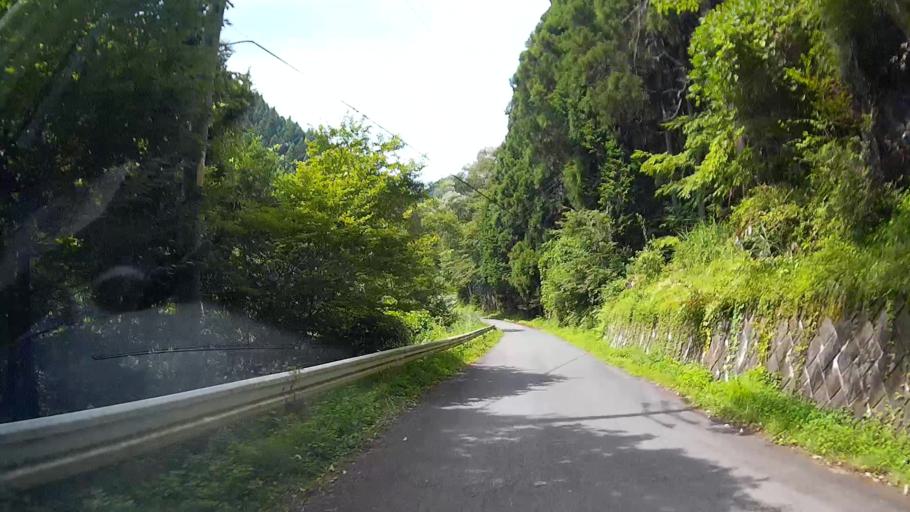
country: JP
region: Saitama
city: Chichibu
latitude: 35.9059
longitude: 139.0966
